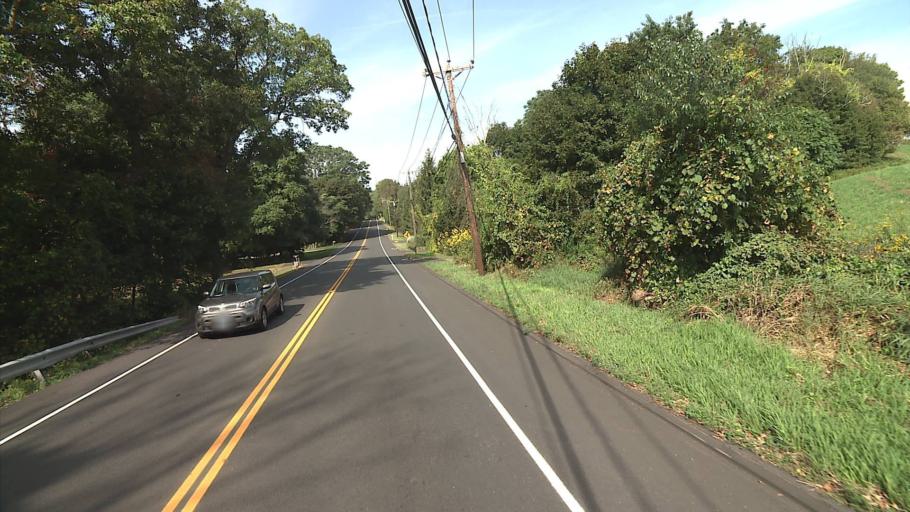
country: US
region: Connecticut
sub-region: Fairfield County
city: Newtown
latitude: 41.3930
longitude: -73.2280
